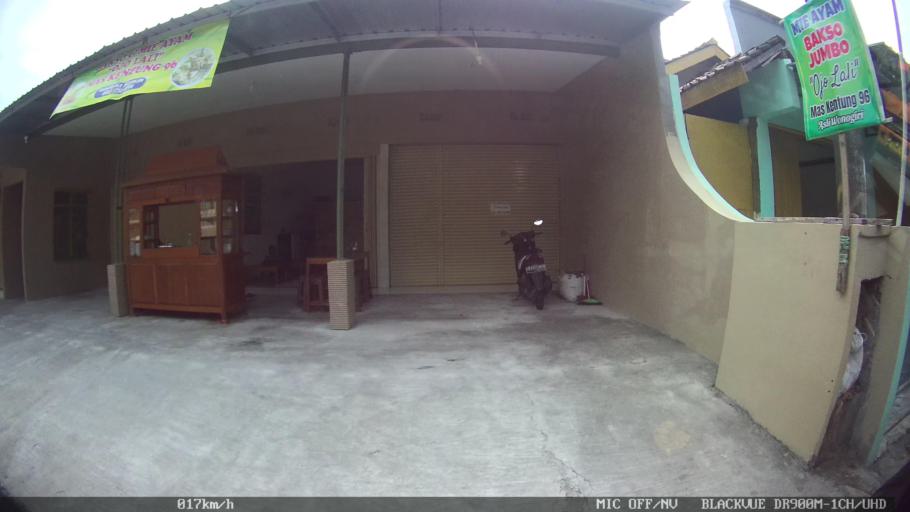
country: ID
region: Central Java
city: Candi Prambanan
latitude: -7.7557
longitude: 110.4805
